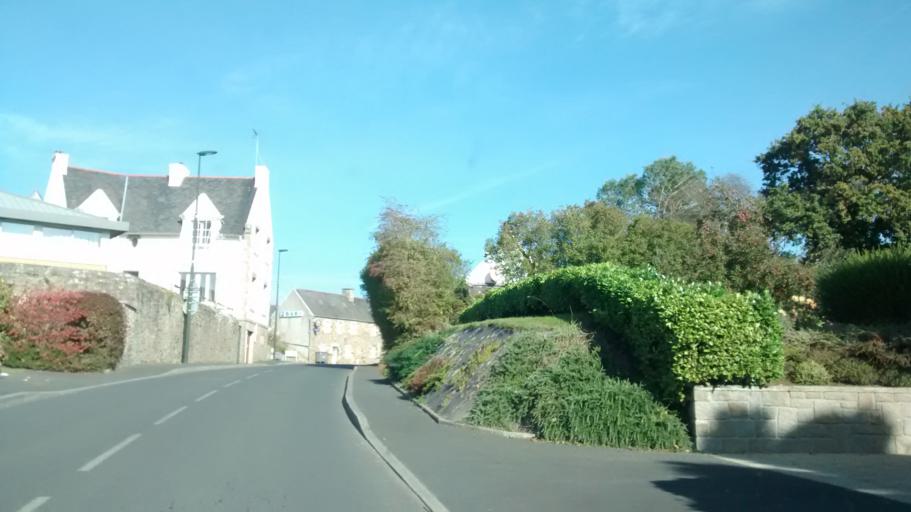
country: FR
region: Brittany
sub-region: Departement des Cotes-d'Armor
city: Lannion
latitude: 48.7504
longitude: -3.4462
